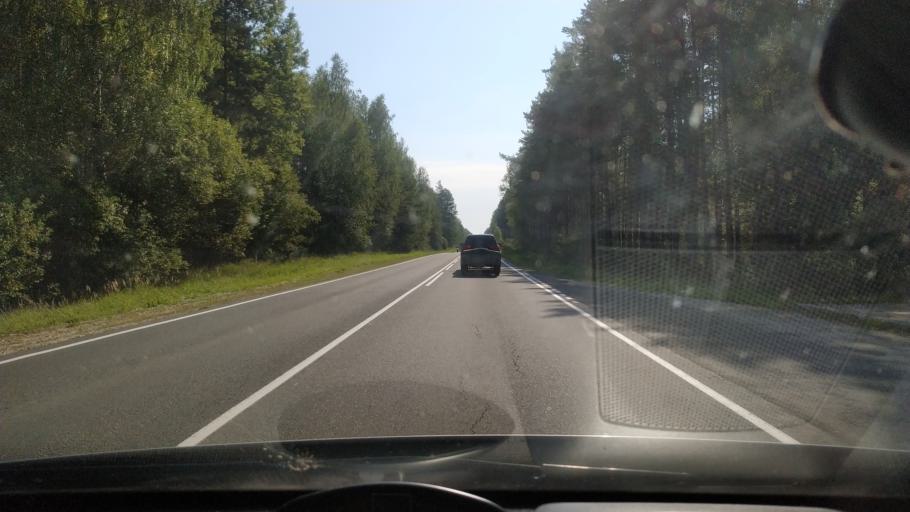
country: RU
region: Rjazan
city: Spas-Klepiki
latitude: 55.2237
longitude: 40.0725
